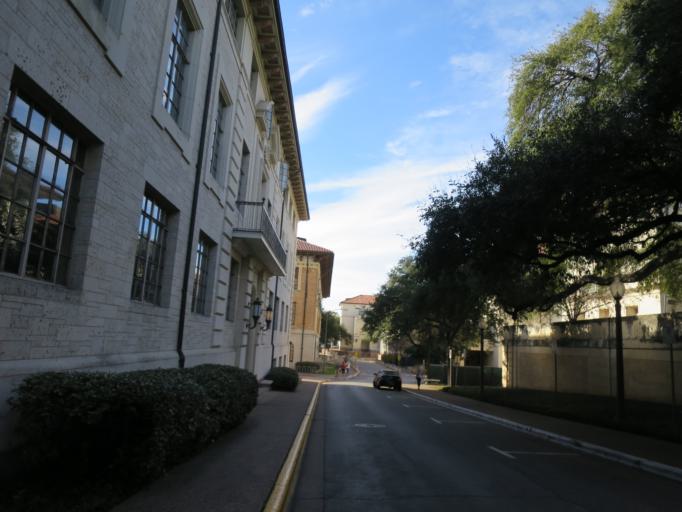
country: US
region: Texas
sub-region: Travis County
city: Austin
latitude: 30.2850
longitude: -97.7398
